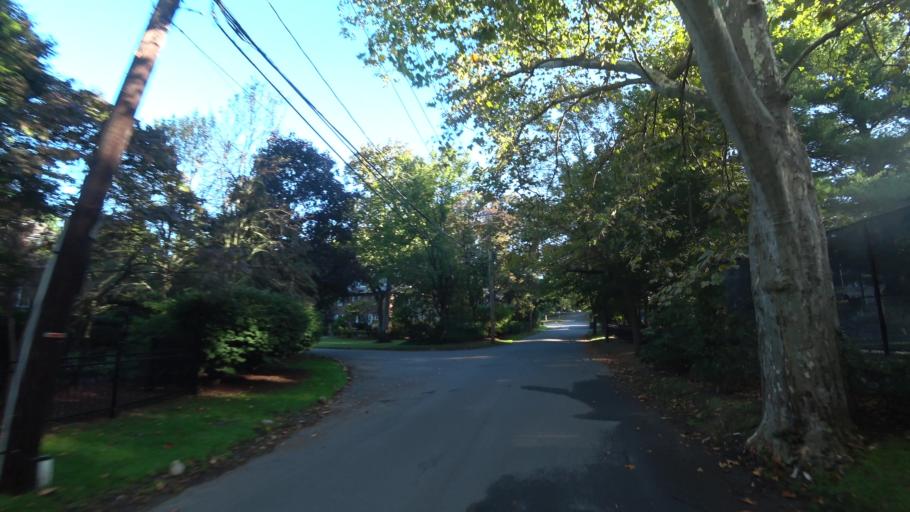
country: US
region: Massachusetts
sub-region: Middlesex County
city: Newton
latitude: 42.3297
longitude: -71.1729
